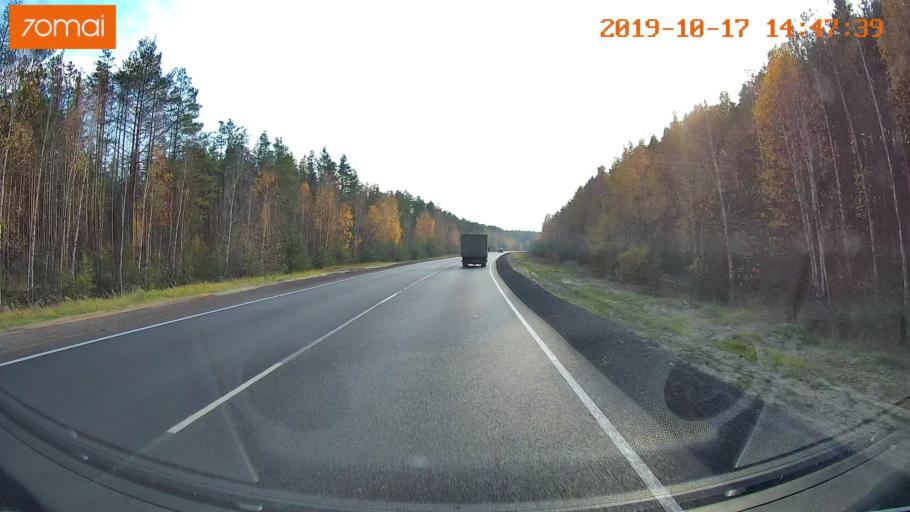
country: RU
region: Rjazan
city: Solotcha
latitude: 54.7685
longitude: 39.8588
